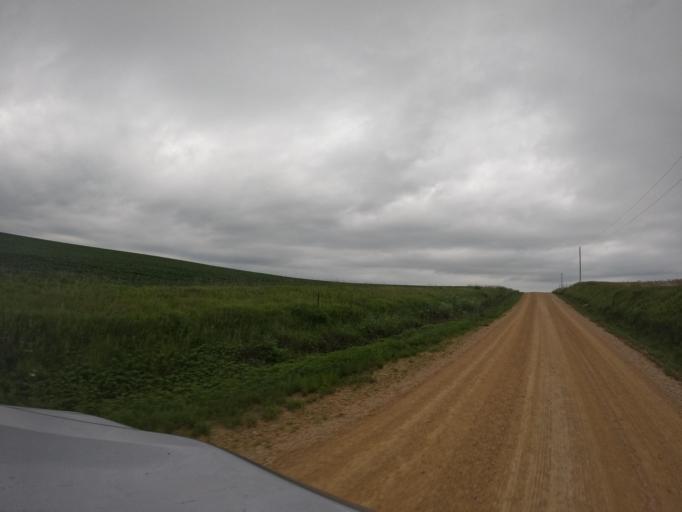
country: US
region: Iowa
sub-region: Jackson County
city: Maquoketa
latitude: 41.9442
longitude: -90.6455
